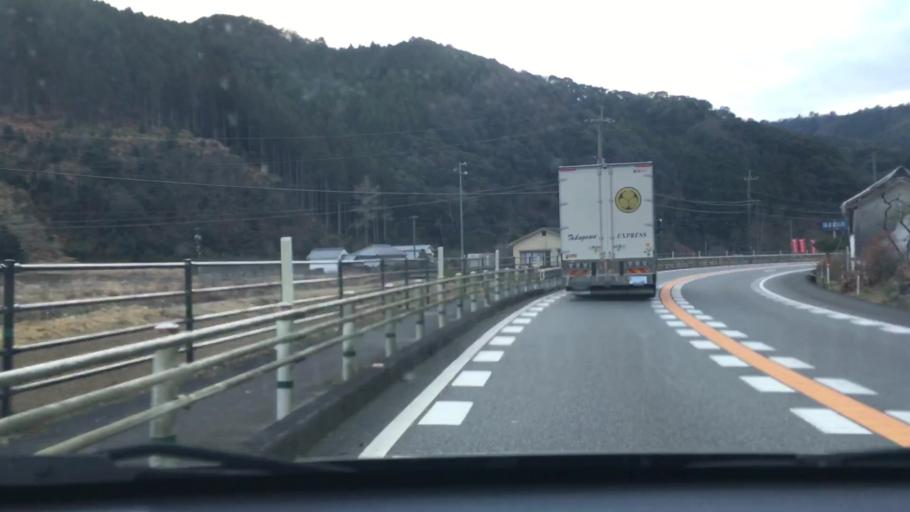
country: JP
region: Oita
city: Usuki
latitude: 33.0057
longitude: 131.7368
